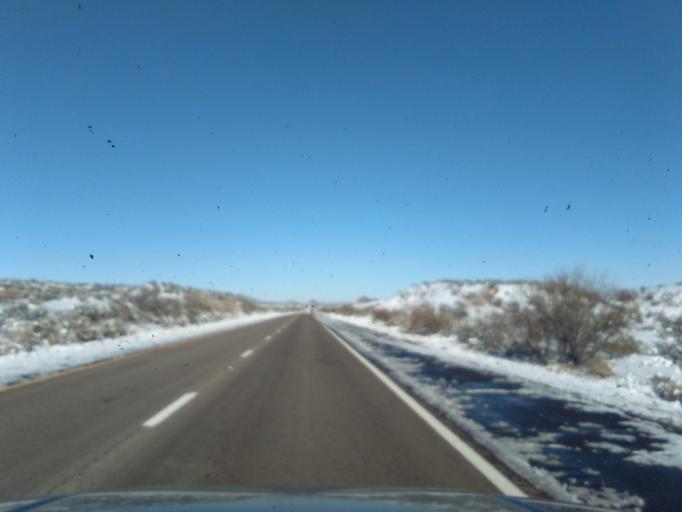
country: US
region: New Mexico
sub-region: Socorro County
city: Socorro
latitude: 33.6890
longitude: -107.0618
